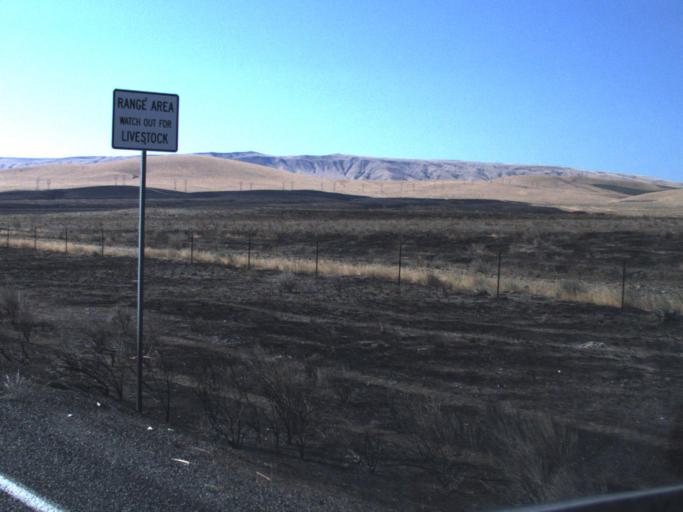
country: US
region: Washington
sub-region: Grant County
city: Desert Aire
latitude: 46.5759
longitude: -119.7281
